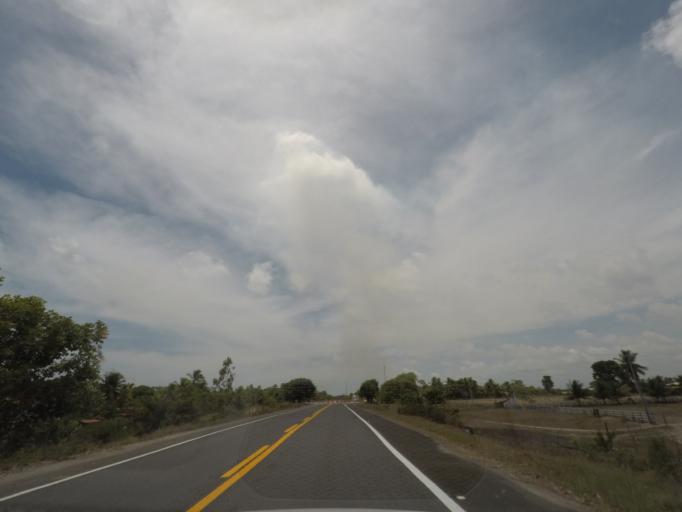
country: BR
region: Bahia
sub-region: Conde
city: Conde
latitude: -11.7523
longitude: -37.5866
